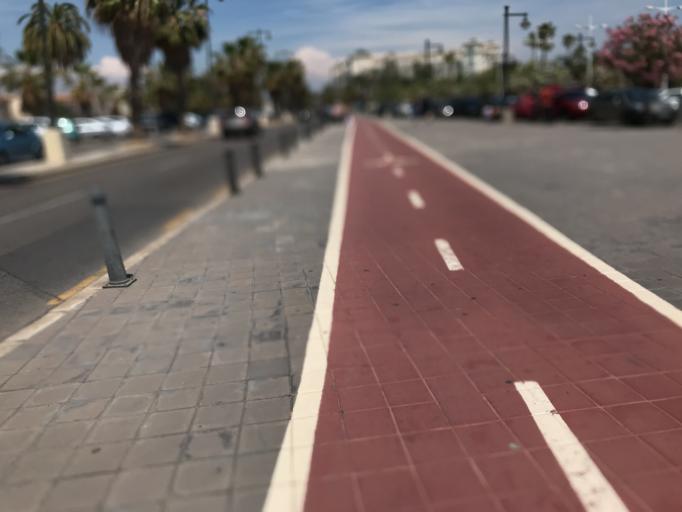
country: ES
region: Valencia
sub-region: Provincia de Valencia
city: Alboraya
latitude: 39.4638
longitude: -0.3248
